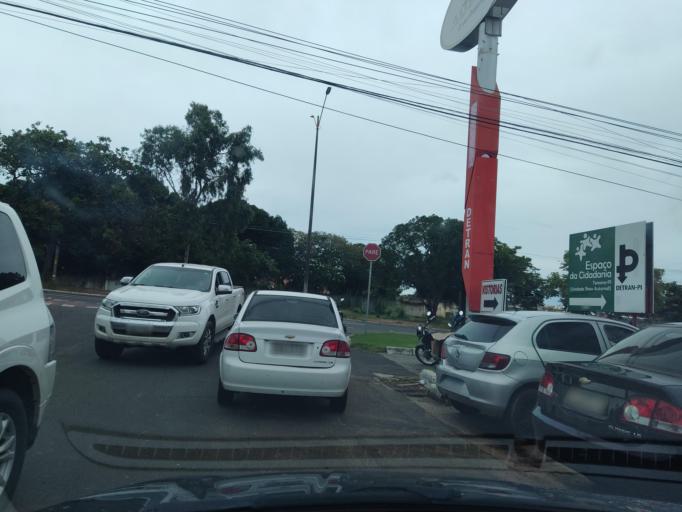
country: BR
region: Piaui
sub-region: Teresina
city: Teresina
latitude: -5.0789
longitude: -42.7533
